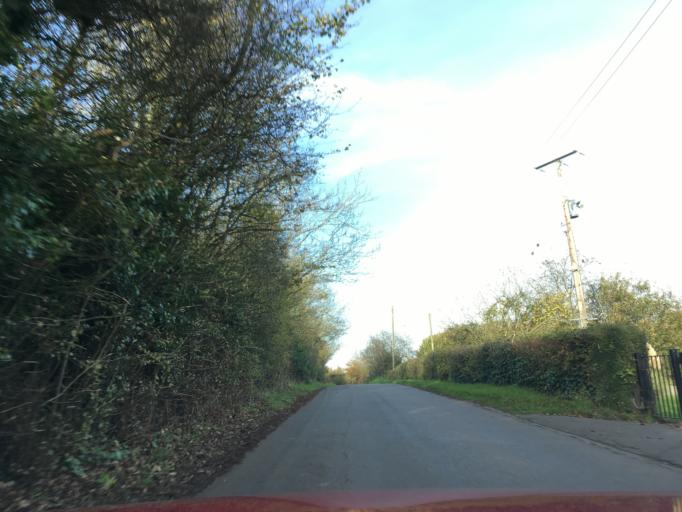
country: GB
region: England
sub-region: South Gloucestershire
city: Tytherington
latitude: 51.6068
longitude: -2.4738
